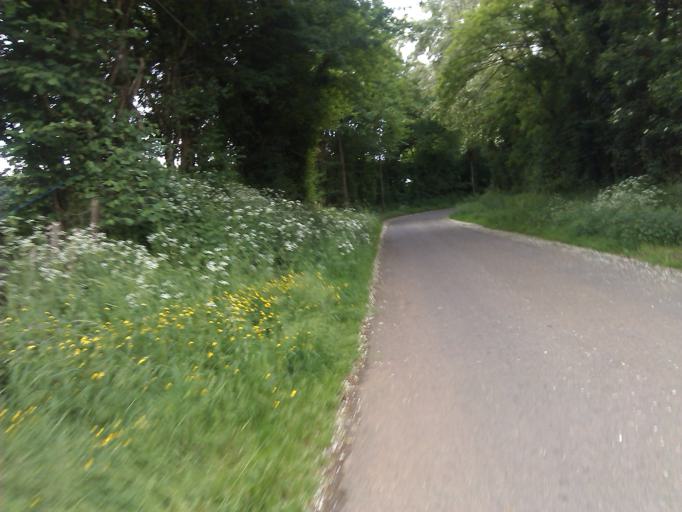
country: FR
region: Poitou-Charentes
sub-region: Departement de la Charente
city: Nanteuil-en-Vallee
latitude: 45.9854
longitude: 0.3507
